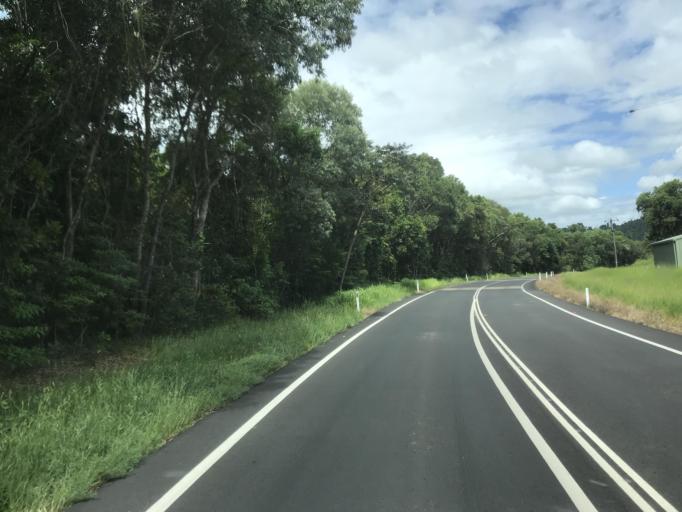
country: AU
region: Queensland
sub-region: Cassowary Coast
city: Innisfail
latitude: -17.8698
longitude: 146.0858
